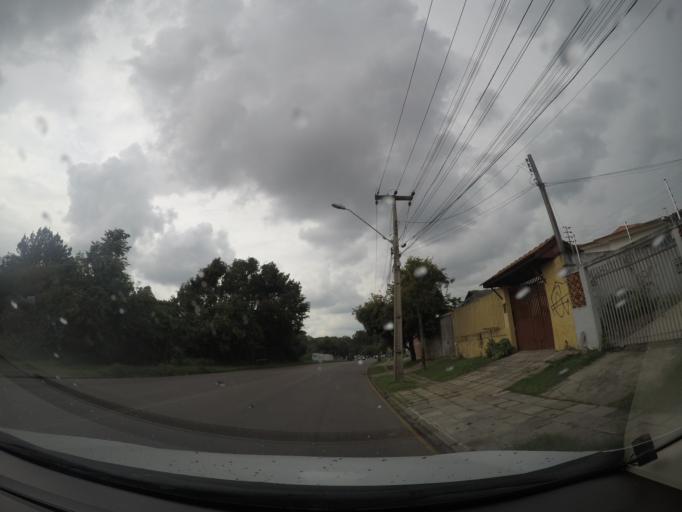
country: BR
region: Parana
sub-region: Sao Jose Dos Pinhais
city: Sao Jose dos Pinhais
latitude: -25.5249
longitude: -49.2489
